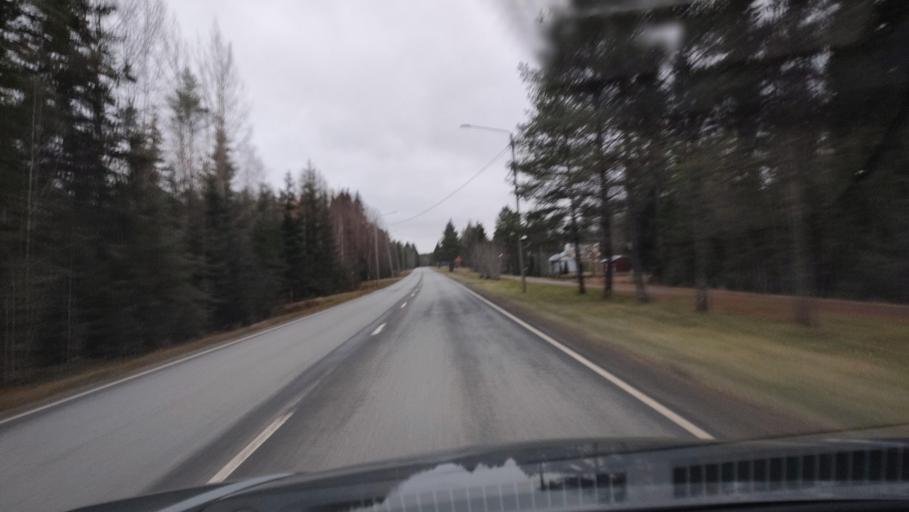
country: FI
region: Southern Ostrobothnia
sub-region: Suupohja
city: Kauhajoki
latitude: 62.4007
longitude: 22.1590
